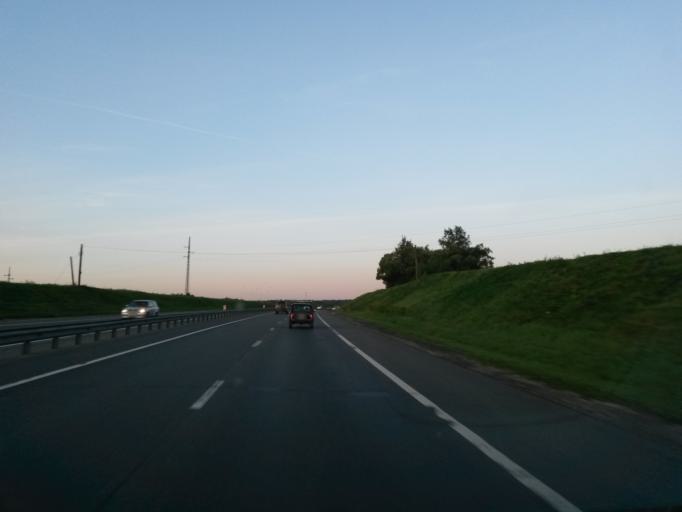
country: RU
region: Moskovskaya
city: Sergiyev Posad
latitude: 56.2744
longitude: 38.1993
